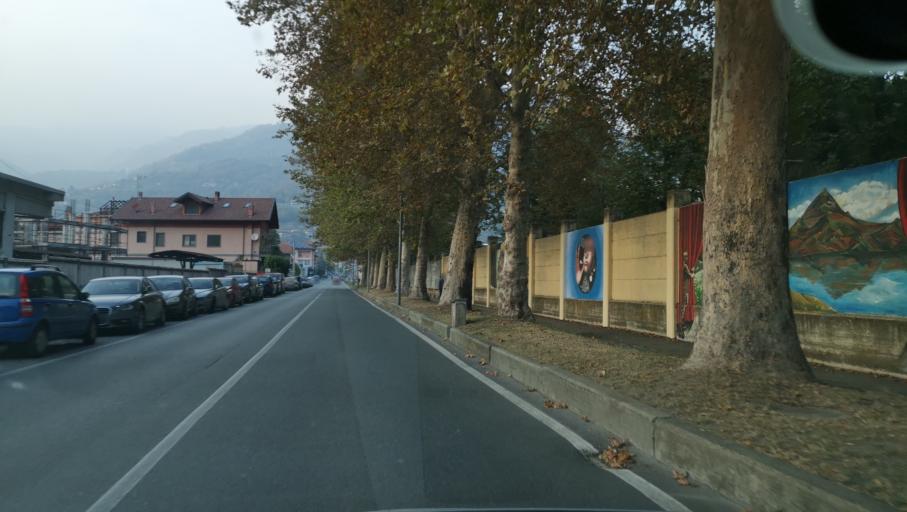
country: IT
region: Piedmont
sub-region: Provincia di Torino
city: Condove
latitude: 45.1119
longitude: 7.3139
